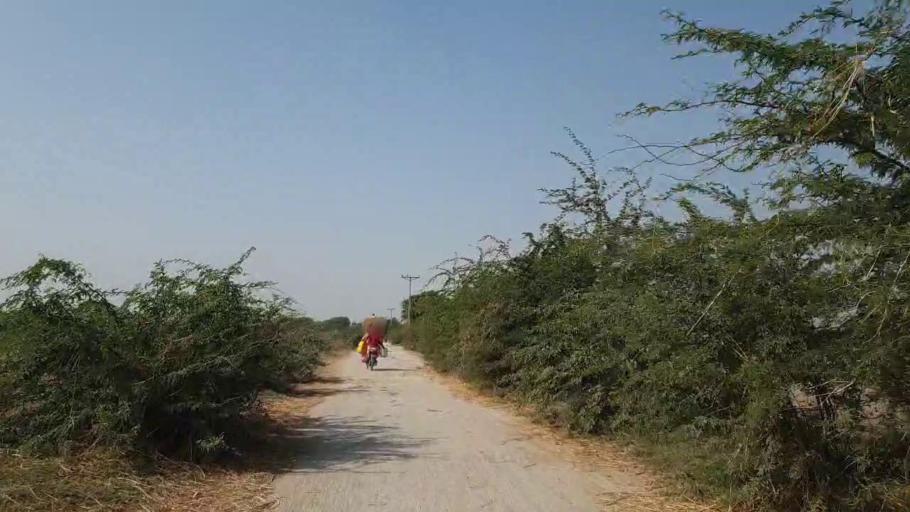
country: PK
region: Sindh
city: Bulri
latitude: 24.9582
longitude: 68.3326
